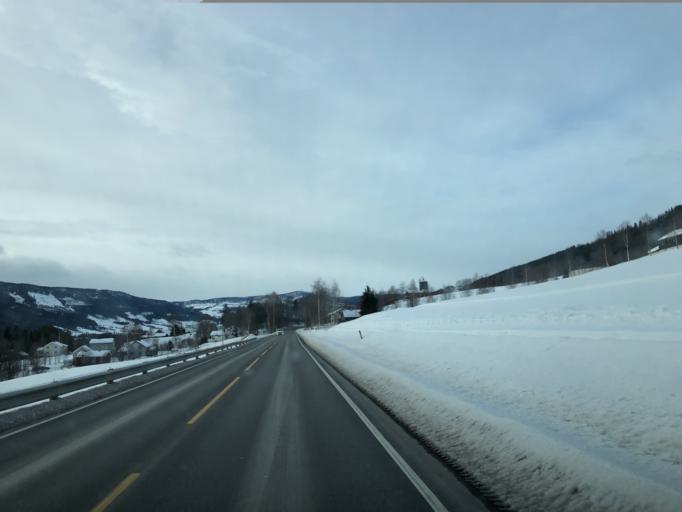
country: NO
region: Oppland
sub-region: Gausdal
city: Segalstad bru
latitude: 61.2367
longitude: 10.2058
